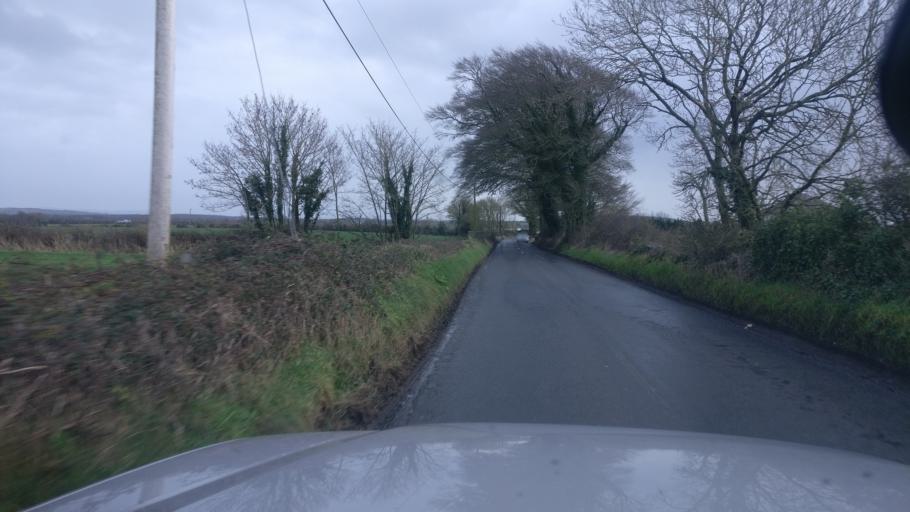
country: IE
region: Munster
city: Nenagh Bridge
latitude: 52.9886
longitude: -8.1169
